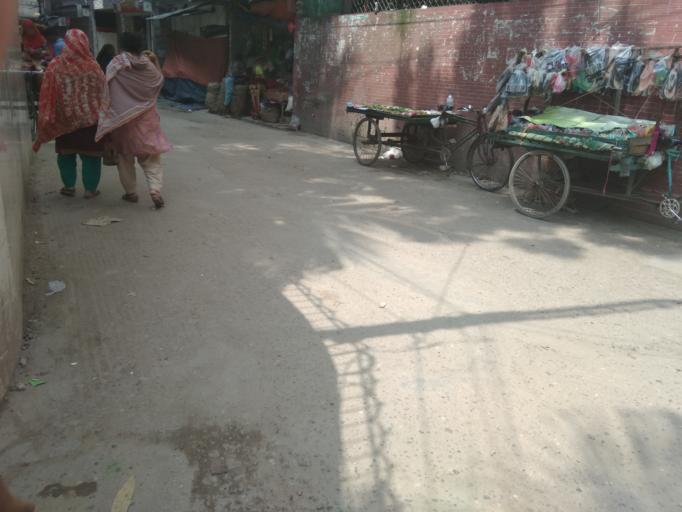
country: BD
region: Dhaka
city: Azimpur
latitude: 23.8050
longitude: 90.3728
